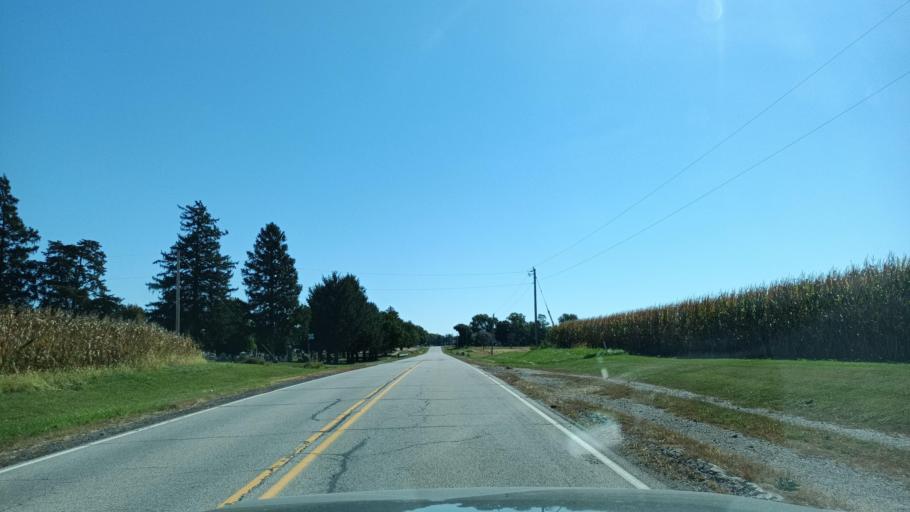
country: US
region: Illinois
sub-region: Peoria County
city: Elmwood
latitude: 40.8433
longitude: -89.8995
